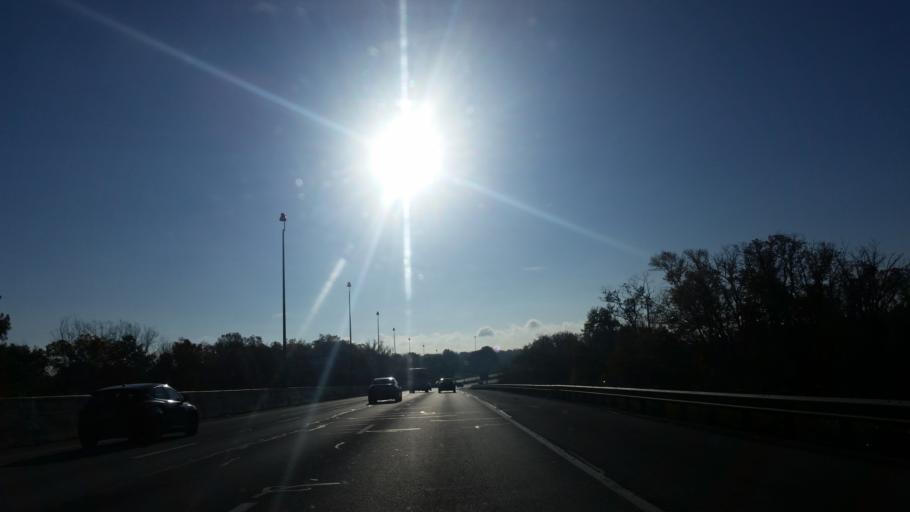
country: US
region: Ohio
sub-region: Summit County
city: Fairlawn
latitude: 41.1046
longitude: -81.5952
